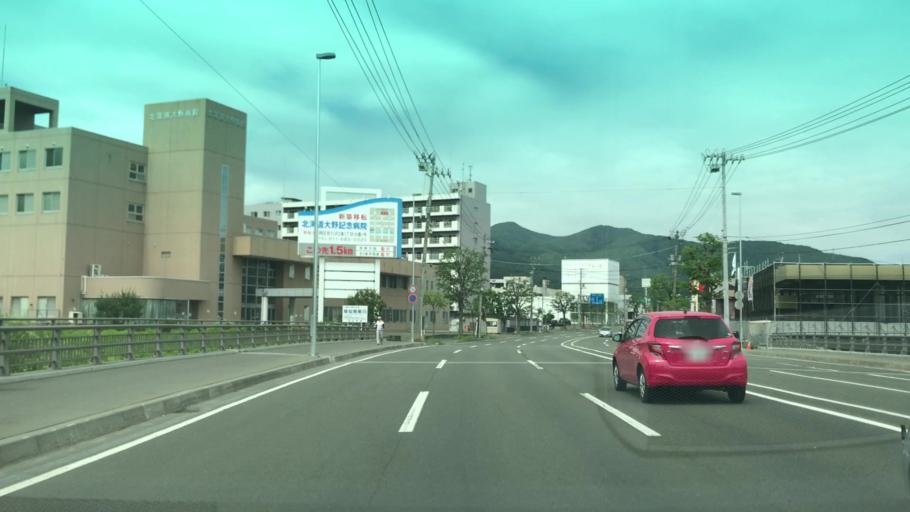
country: JP
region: Hokkaido
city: Sapporo
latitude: 43.0713
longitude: 141.2841
